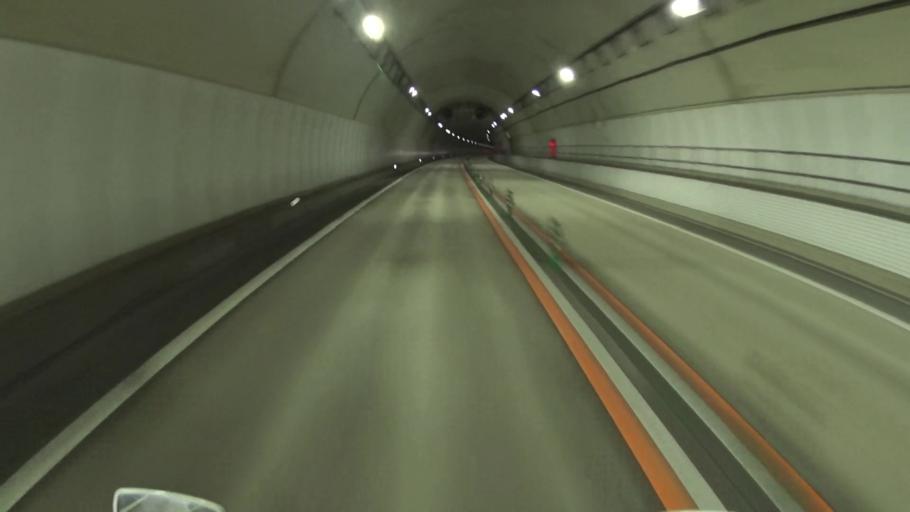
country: JP
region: Kyoto
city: Ayabe
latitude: 35.3958
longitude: 135.2352
